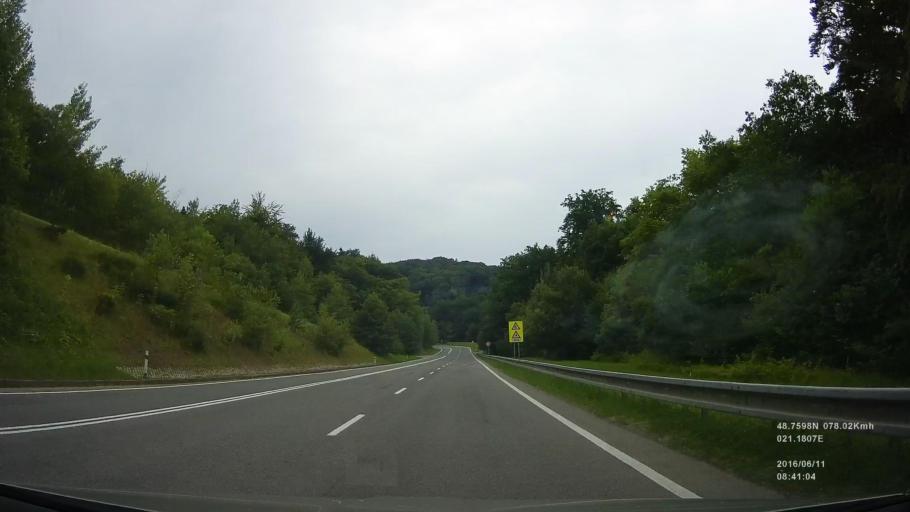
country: SK
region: Kosicky
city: Kosice
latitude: 48.7442
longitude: 21.2374
